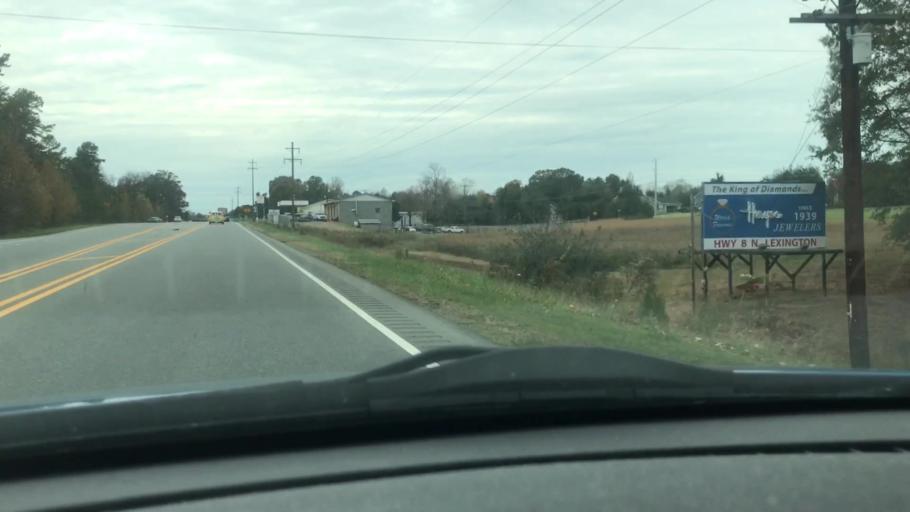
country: US
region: North Carolina
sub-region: Davidson County
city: Thomasville
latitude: 35.7703
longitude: -80.0967
